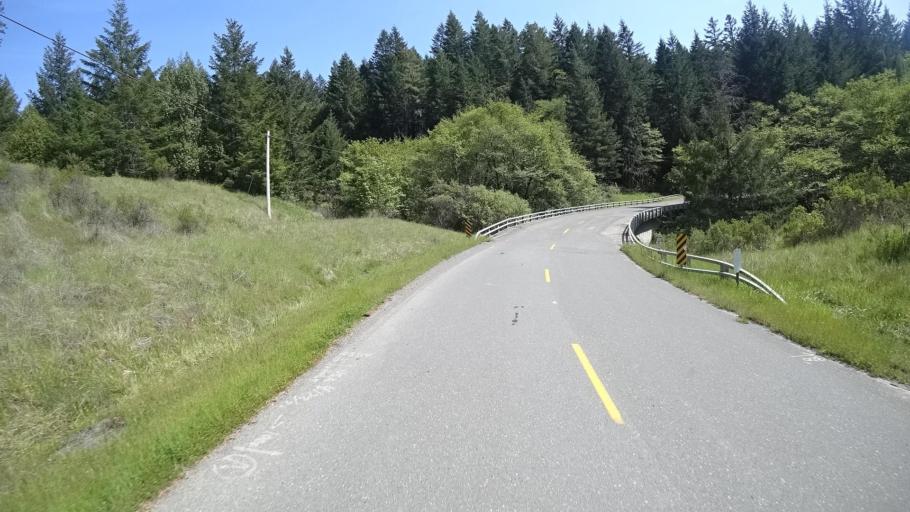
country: US
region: California
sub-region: Humboldt County
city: Redway
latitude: 40.3675
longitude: -123.7290
